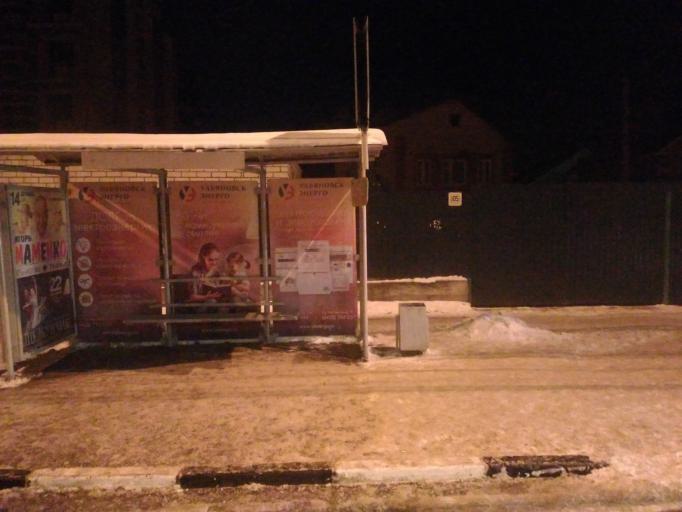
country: RU
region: Ulyanovsk
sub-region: Ulyanovskiy Rayon
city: Ulyanovsk
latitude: 54.3341
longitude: 48.3996
